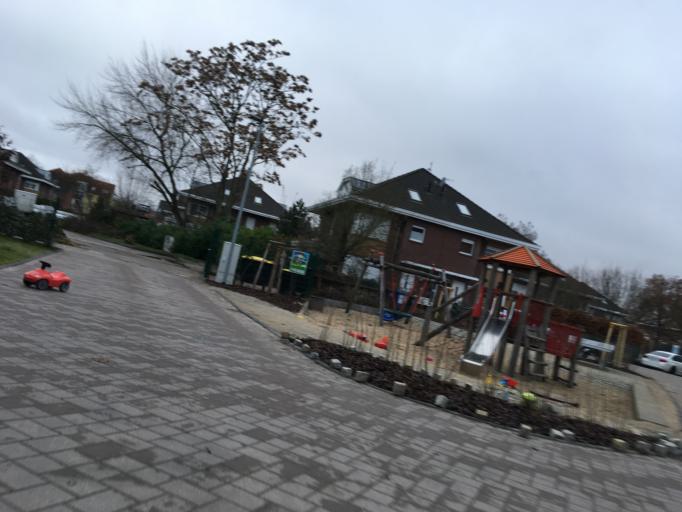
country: DE
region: Berlin
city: Wilhelmsruh
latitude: 52.5861
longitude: 13.3770
